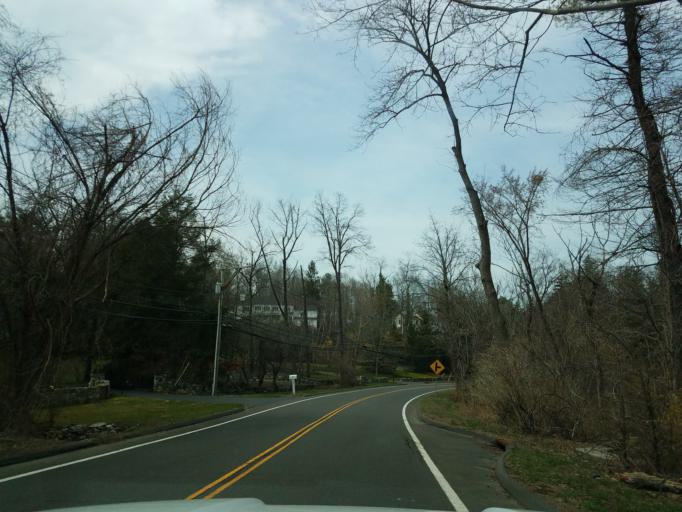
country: US
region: Connecticut
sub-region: Fairfield County
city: Glenville
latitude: 41.0771
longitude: -73.6415
